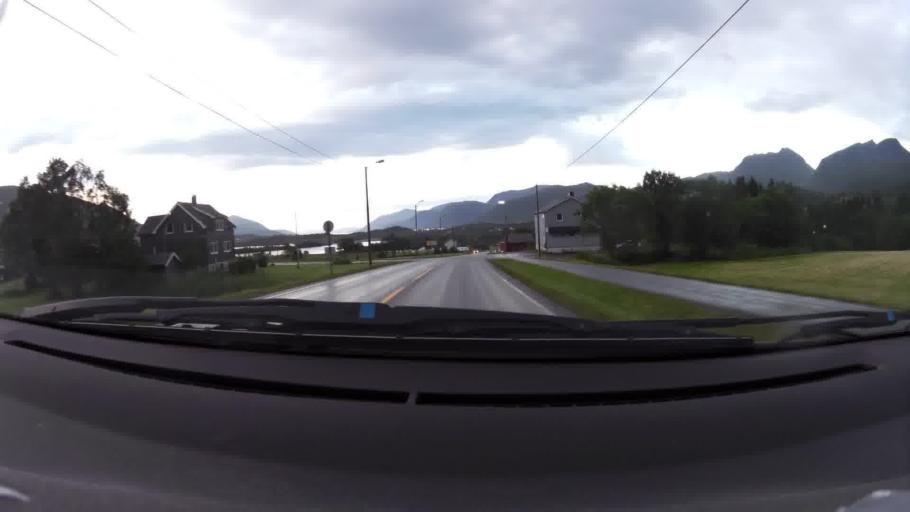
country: NO
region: More og Romsdal
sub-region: Eide
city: Eide
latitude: 62.8942
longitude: 7.3860
